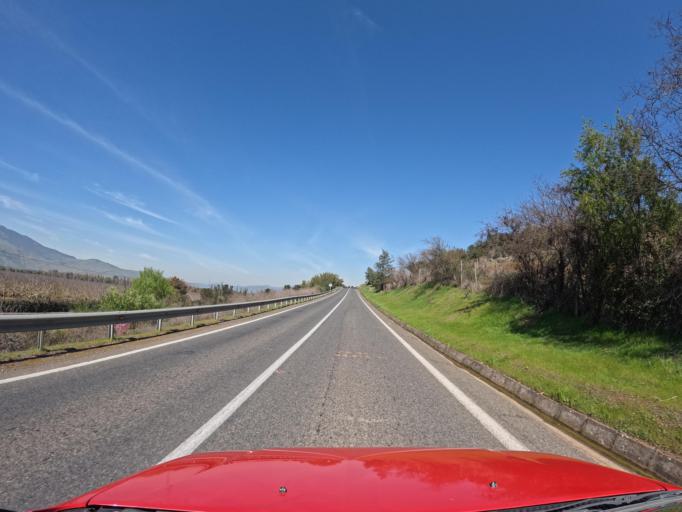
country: CL
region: Maule
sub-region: Provincia de Curico
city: Rauco
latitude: -35.0654
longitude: -71.6232
